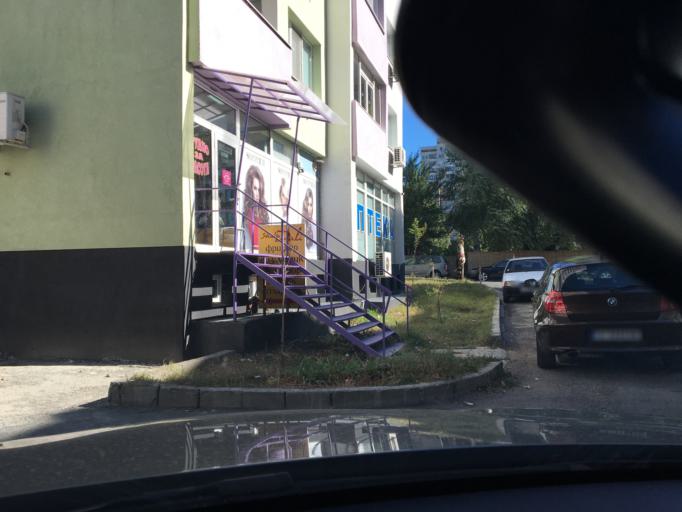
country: BG
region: Burgas
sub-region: Obshtina Burgas
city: Burgas
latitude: 42.5204
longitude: 27.4512
